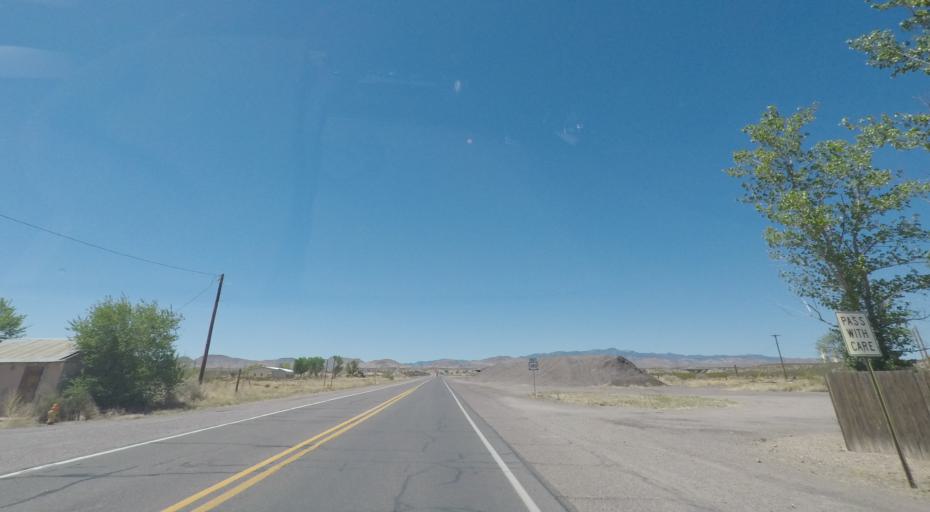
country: US
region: New Mexico
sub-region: Socorro County
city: Socorro
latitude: 33.9177
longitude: -106.8698
